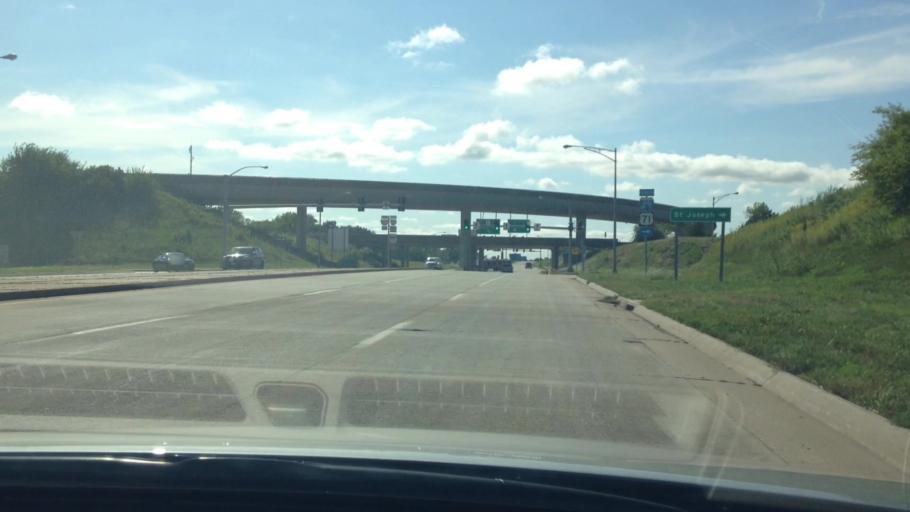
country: US
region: Missouri
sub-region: Platte County
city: Weatherby Lake
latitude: 39.3112
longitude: -94.6857
